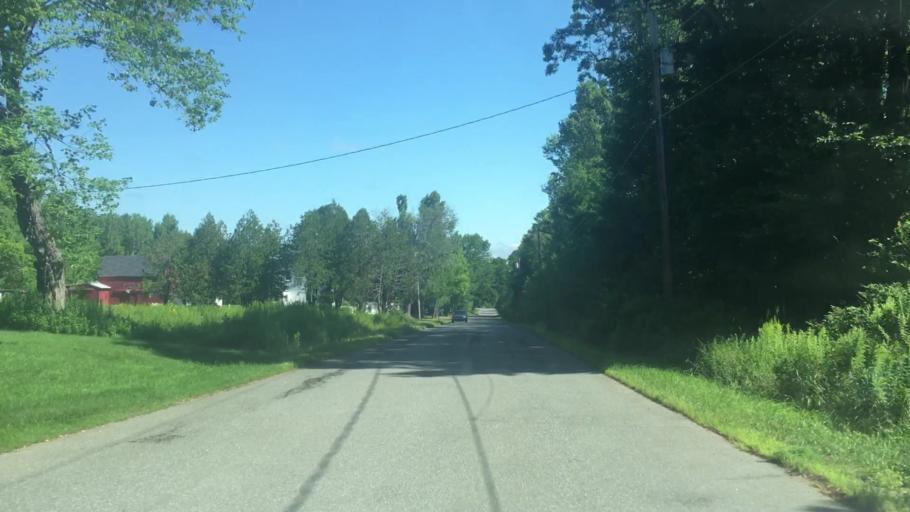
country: US
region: Maine
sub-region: Waldo County
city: Northport
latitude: 44.3791
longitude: -68.9817
